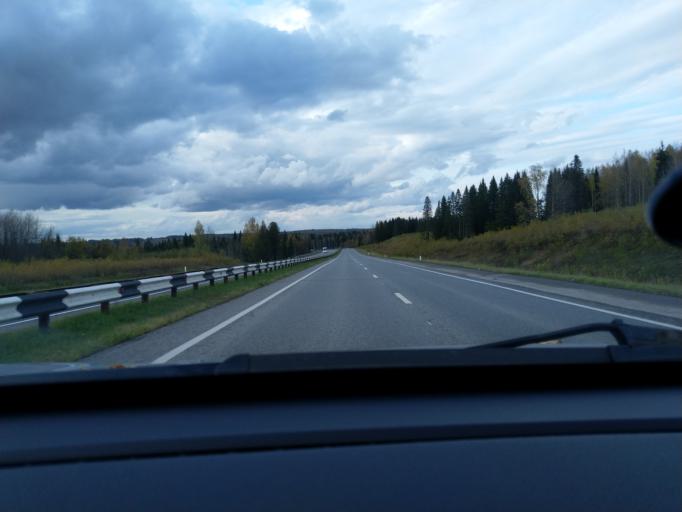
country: RU
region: Perm
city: Polazna
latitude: 58.3029
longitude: 56.4840
